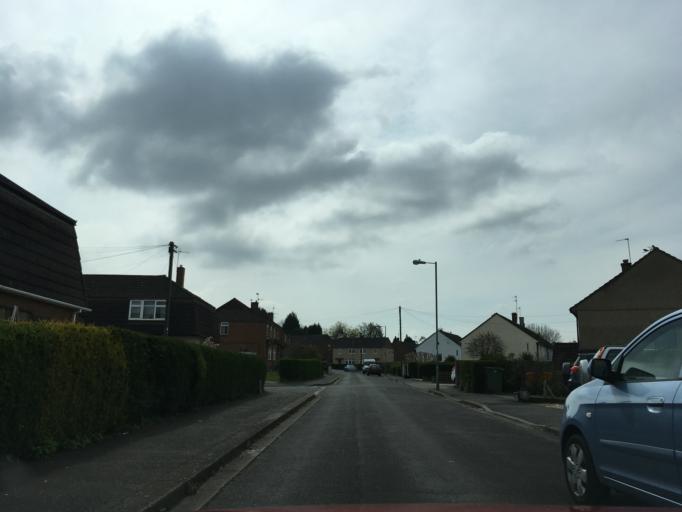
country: GB
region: England
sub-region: South Gloucestershire
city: Almondsbury
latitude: 51.5128
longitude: -2.6019
